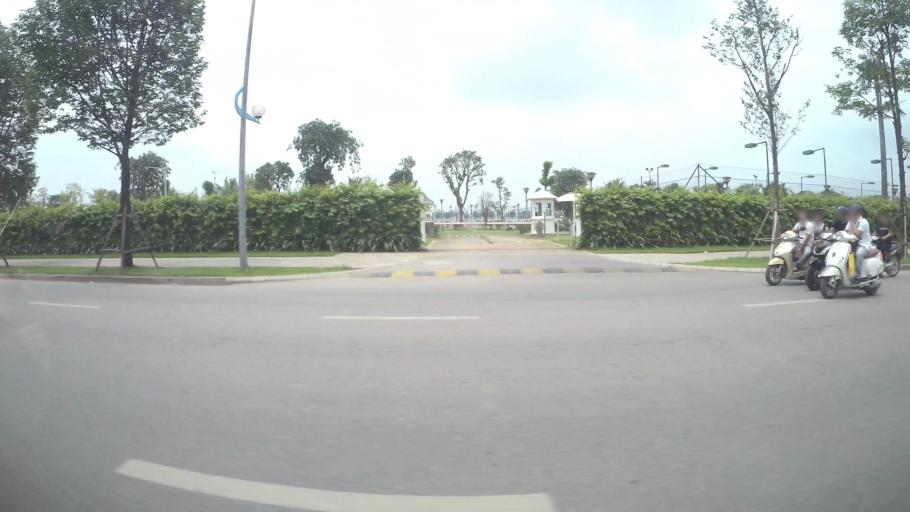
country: VN
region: Ha Noi
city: Trau Quy
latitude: 21.0487
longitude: 105.9091
